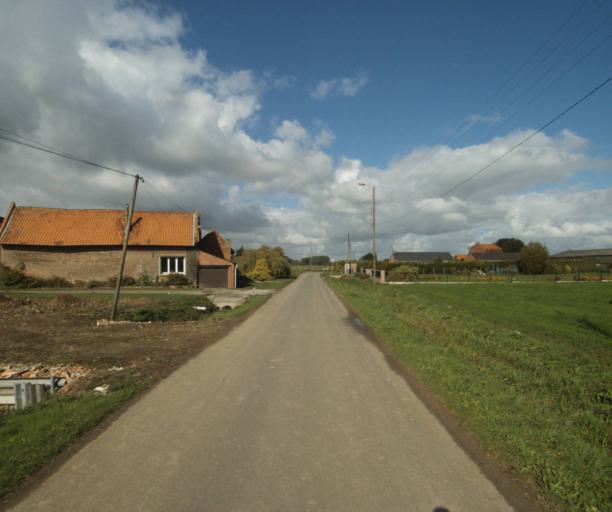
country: FR
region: Nord-Pas-de-Calais
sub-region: Departement du Nord
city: Perenchies
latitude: 50.6906
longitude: 2.9624
